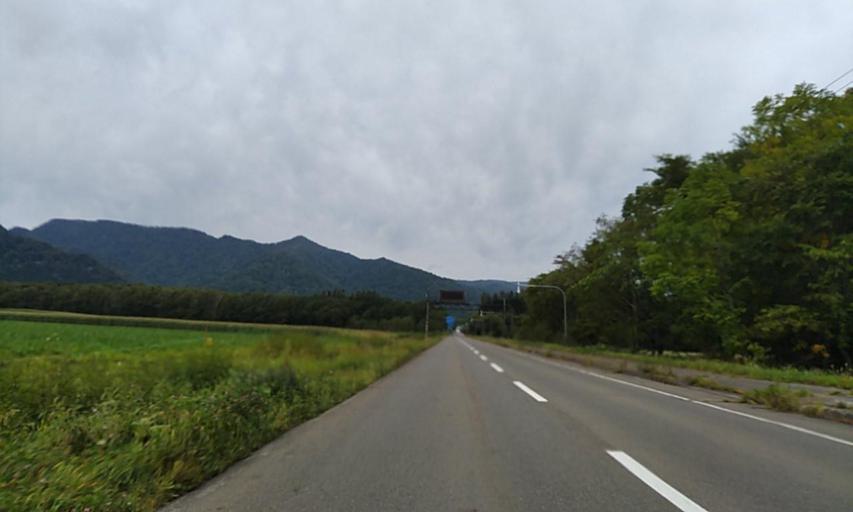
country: JP
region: Hokkaido
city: Bihoro
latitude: 43.5546
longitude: 144.3464
